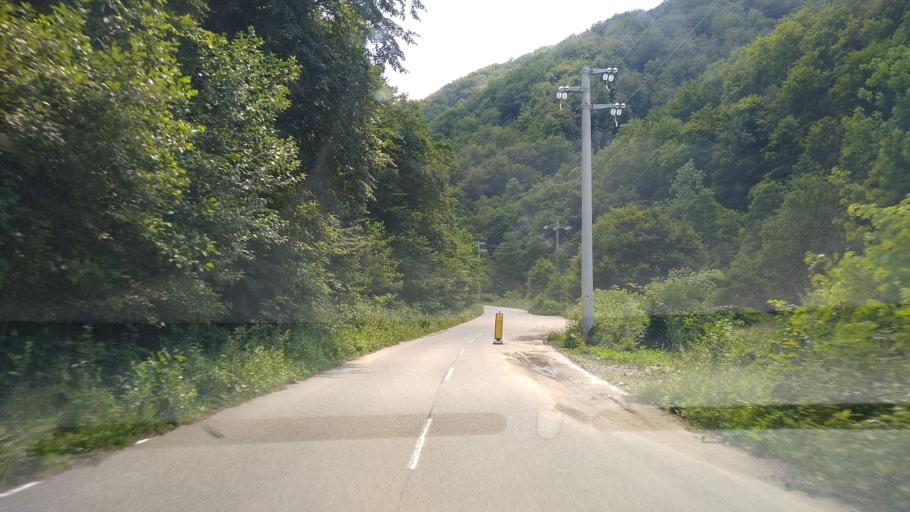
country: RO
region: Hunedoara
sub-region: Comuna Orastioara de Sus
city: Orastioara de Sus
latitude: 45.6682
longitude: 23.1710
